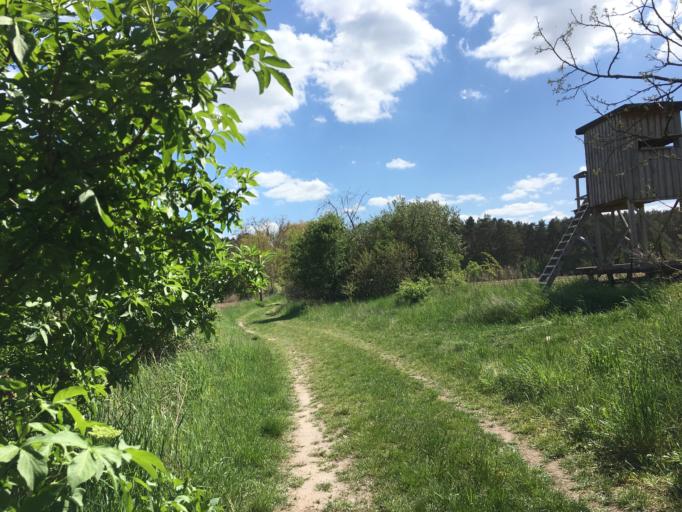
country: DE
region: Brandenburg
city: Rudnitz
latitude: 52.7129
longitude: 13.6587
